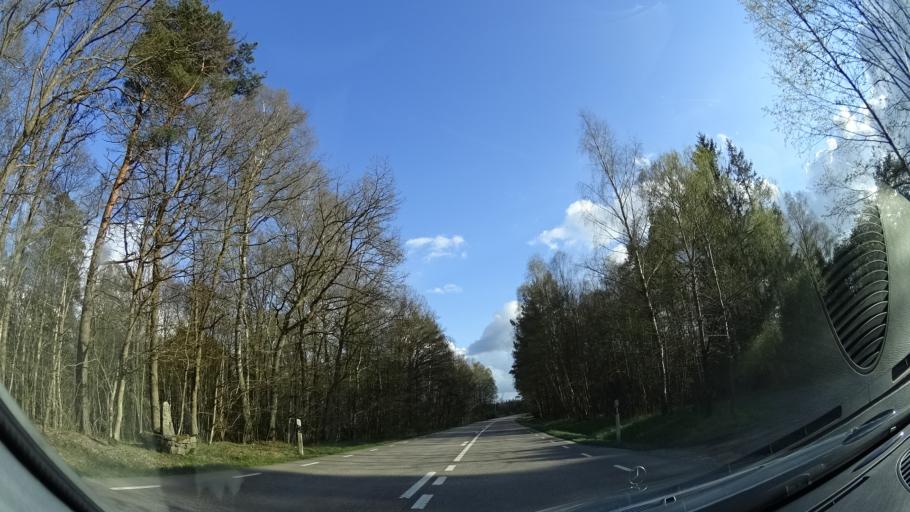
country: SE
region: Skane
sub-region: Klippans Kommun
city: Ljungbyhed
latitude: 56.0998
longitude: 13.2861
